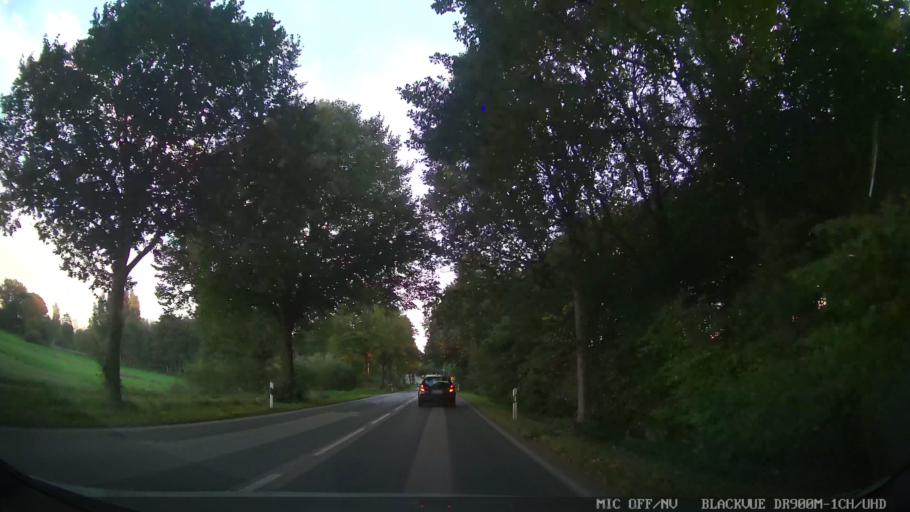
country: DE
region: Schleswig-Holstein
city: Susel
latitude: 54.0483
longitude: 10.6801
